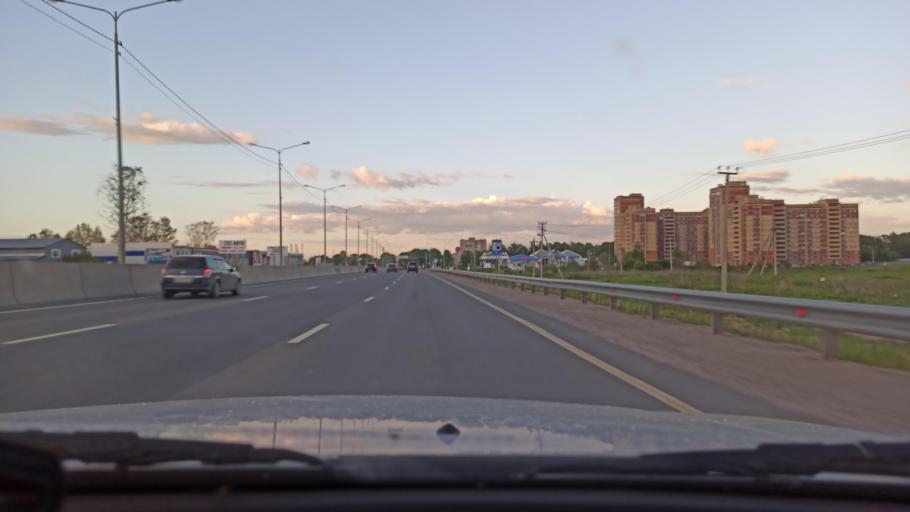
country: RU
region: Vologda
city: Vologda
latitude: 59.2148
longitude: 39.8018
